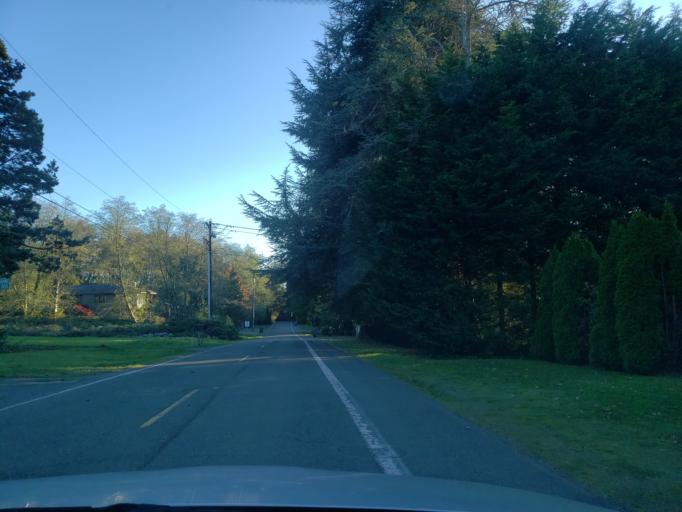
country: US
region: Washington
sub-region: Snohomish County
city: Woodway
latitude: 47.7799
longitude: -122.3883
